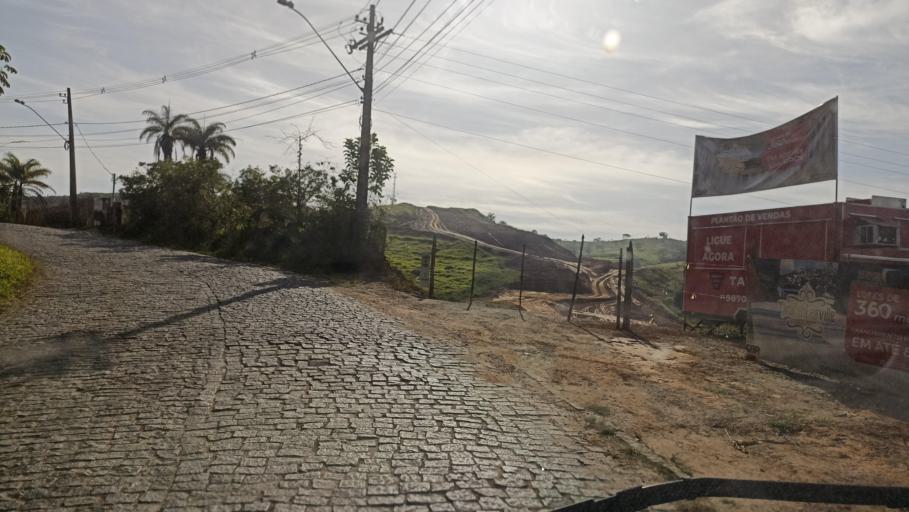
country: BR
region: Minas Gerais
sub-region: Tiradentes
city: Tiradentes
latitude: -21.1209
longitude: -44.1902
